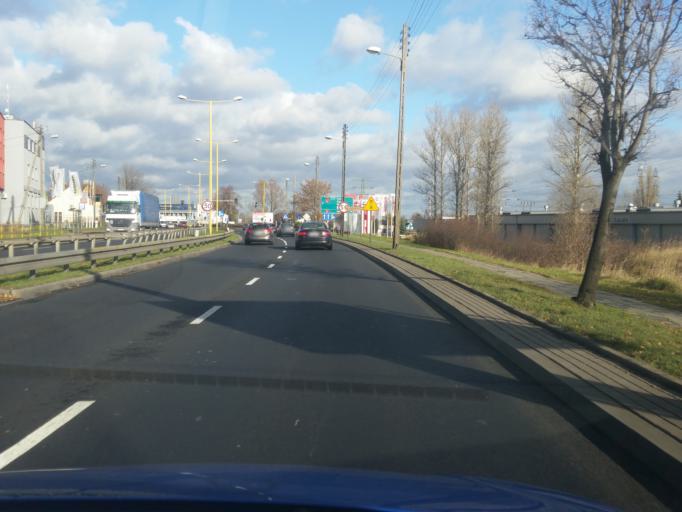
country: PL
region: Silesian Voivodeship
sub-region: Powiat czestochowski
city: Huta Stara B
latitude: 50.7653
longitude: 19.1641
